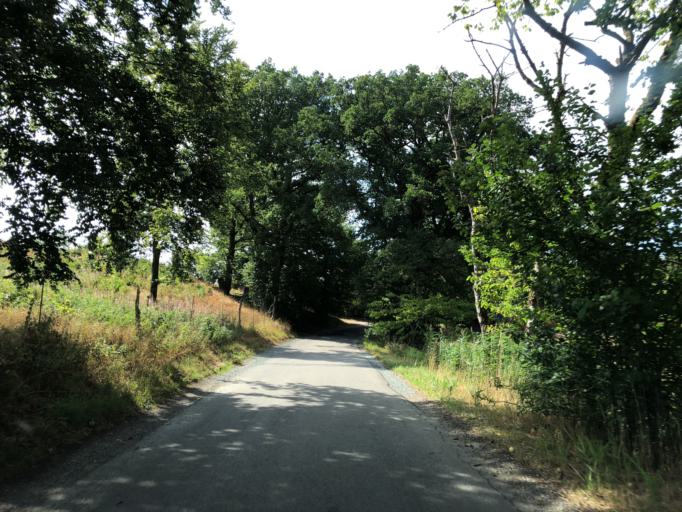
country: DK
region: South Denmark
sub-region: Vejle Kommune
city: Egtved
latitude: 55.6535
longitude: 9.3043
